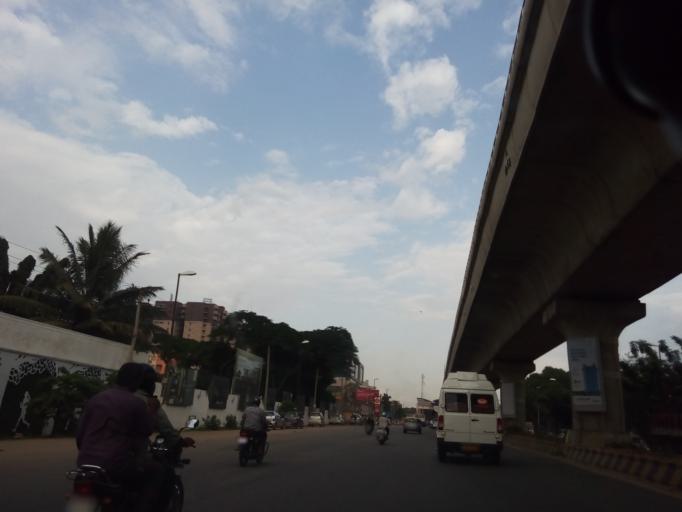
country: IN
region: Karnataka
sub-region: Bangalore Urban
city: Bangalore
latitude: 13.0256
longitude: 77.5457
